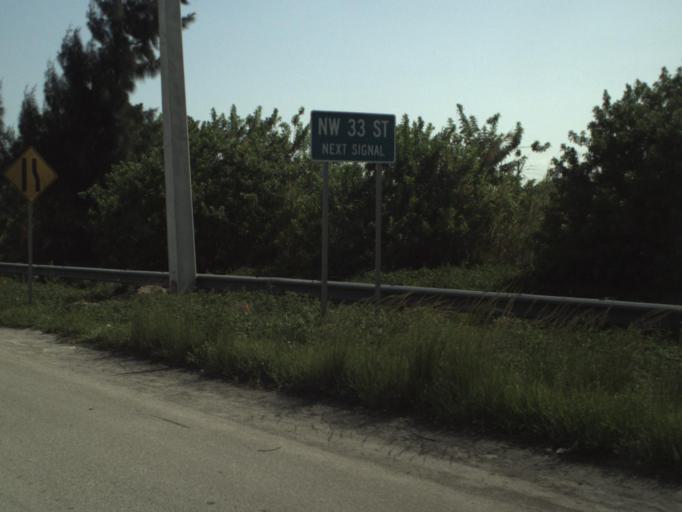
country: US
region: Florida
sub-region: Broward County
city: Tedder
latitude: 26.2731
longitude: -80.1358
